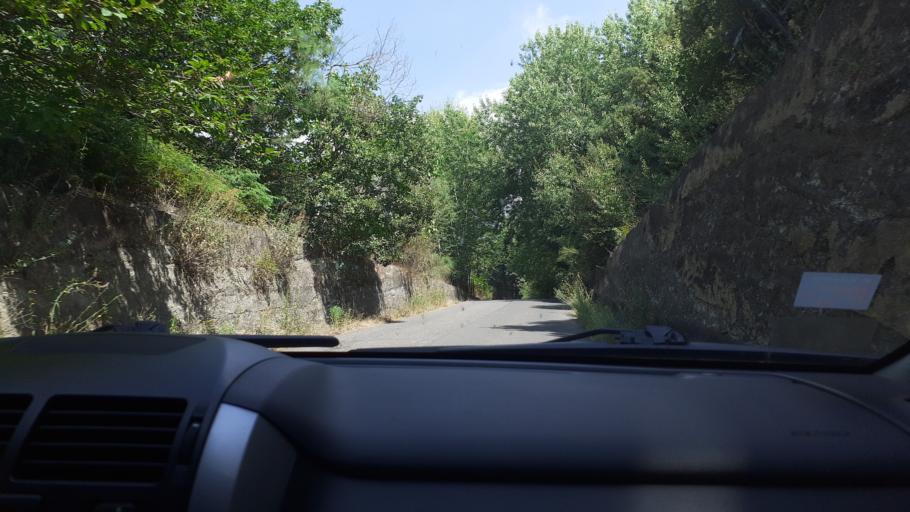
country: IT
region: Sicily
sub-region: Catania
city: Nicolosi
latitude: 37.6403
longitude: 15.0209
